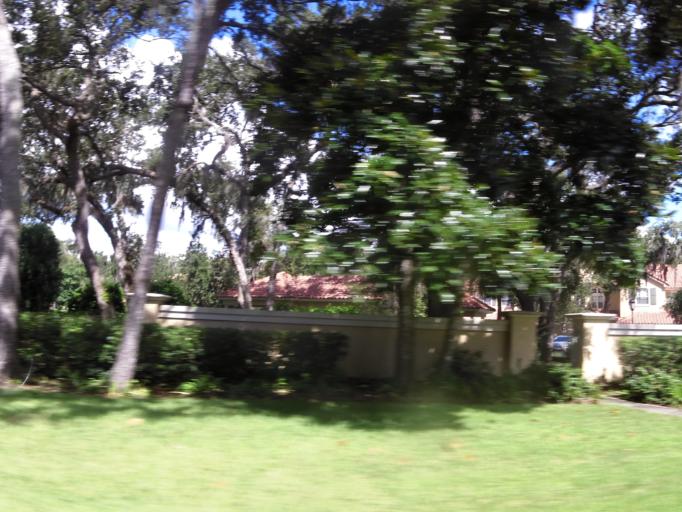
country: US
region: Florida
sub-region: Nassau County
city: Fernandina Beach
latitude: 30.5755
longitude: -81.4509
